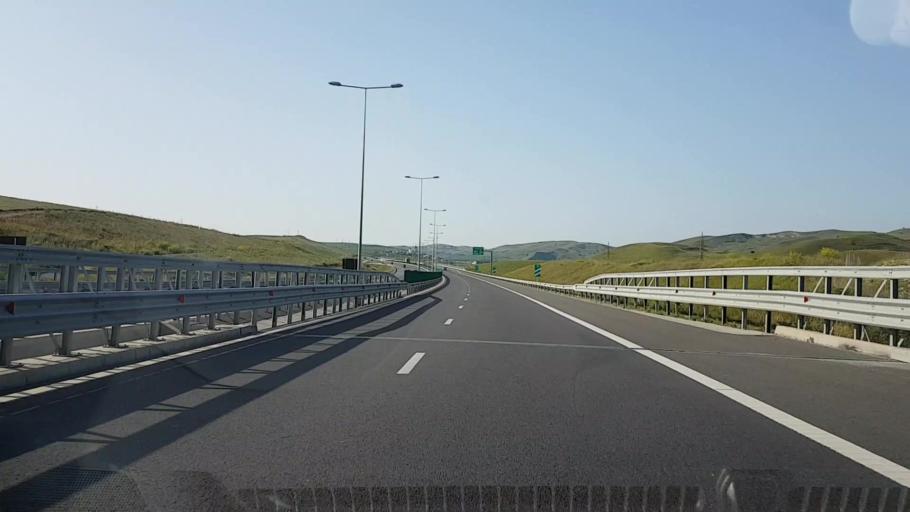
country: RO
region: Alba
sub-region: Comuna Unirea
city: Unirea
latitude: 46.4135
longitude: 23.8010
